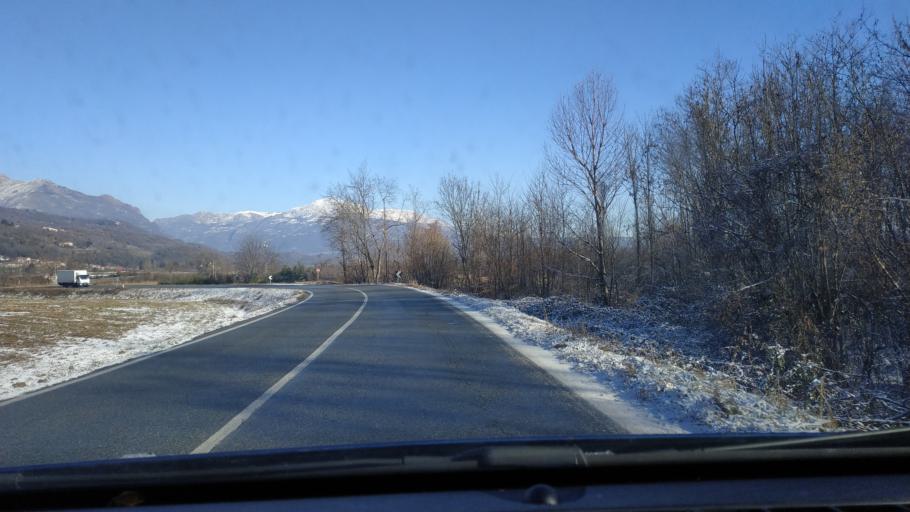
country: IT
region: Piedmont
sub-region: Provincia di Torino
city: Parella
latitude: 45.4205
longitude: 7.7985
